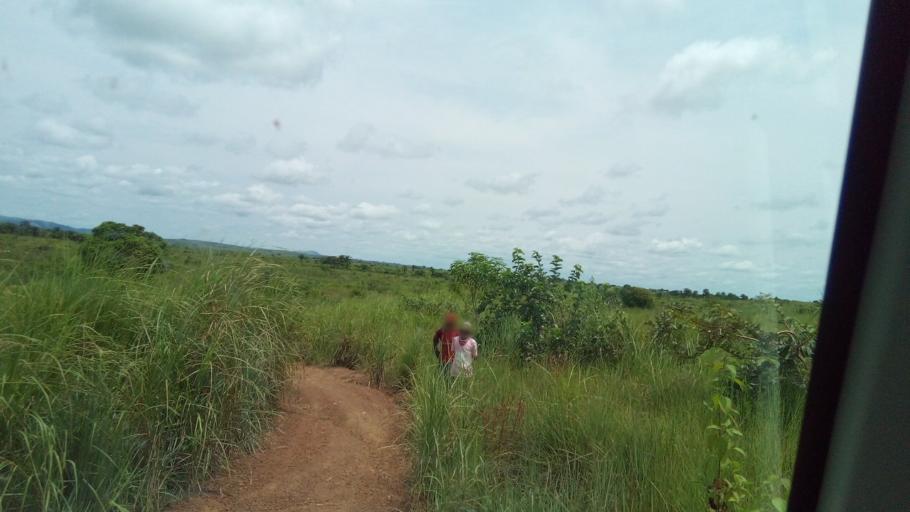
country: AO
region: Zaire
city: Mbanza Congo
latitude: -5.7851
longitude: 13.9913
